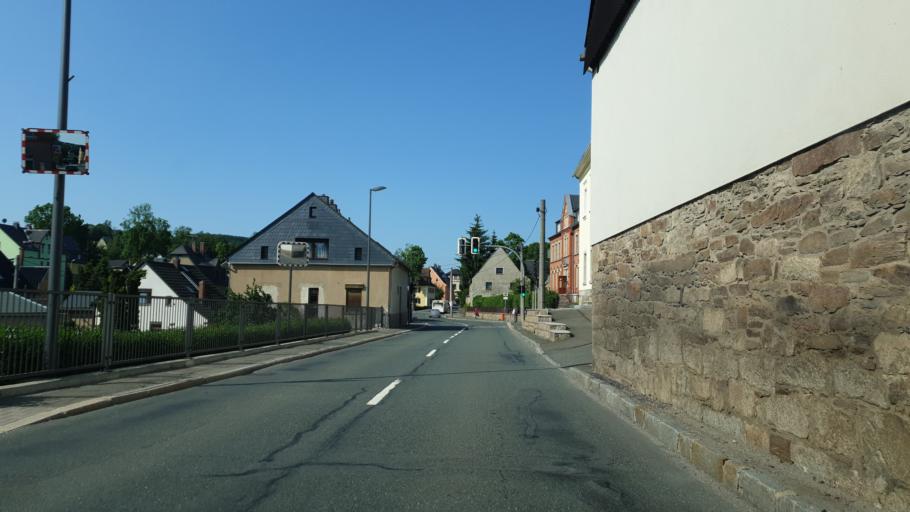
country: DE
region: Saxony
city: Zschorlau
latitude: 50.5694
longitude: 12.6520
